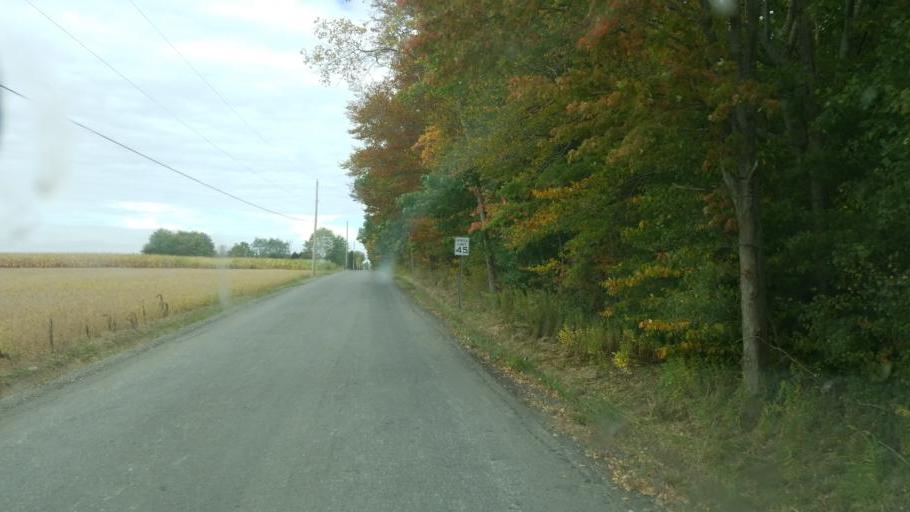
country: US
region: Pennsylvania
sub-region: Mercer County
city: Stoneboro
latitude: 41.3699
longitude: -80.2433
